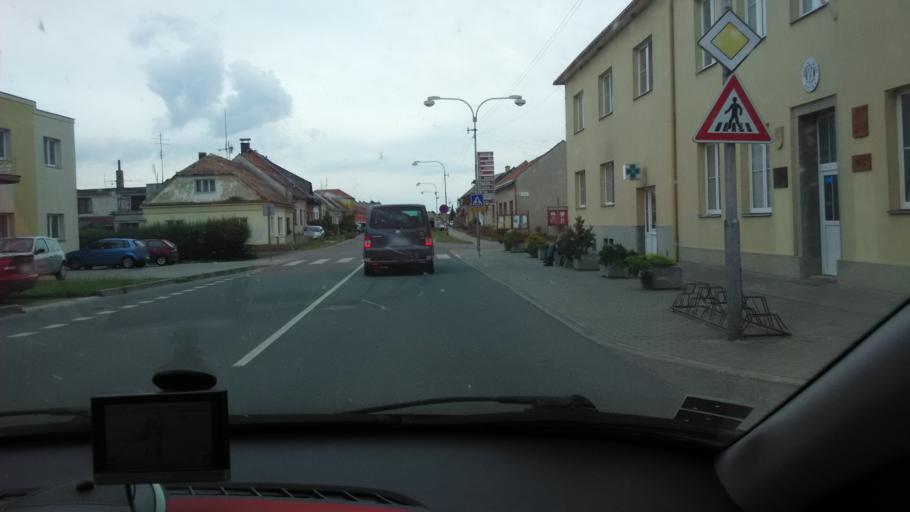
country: CZ
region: South Moravian
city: Kostice
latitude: 48.7462
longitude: 16.9814
